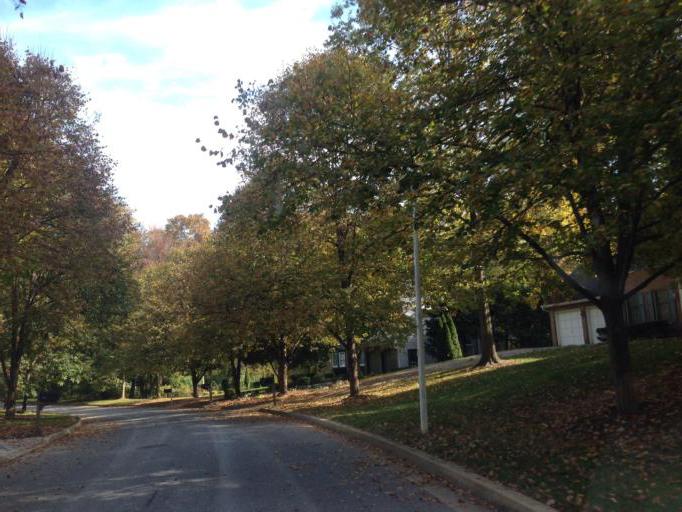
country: US
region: Maryland
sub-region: Howard County
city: Ellicott City
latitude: 39.2860
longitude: -76.8324
